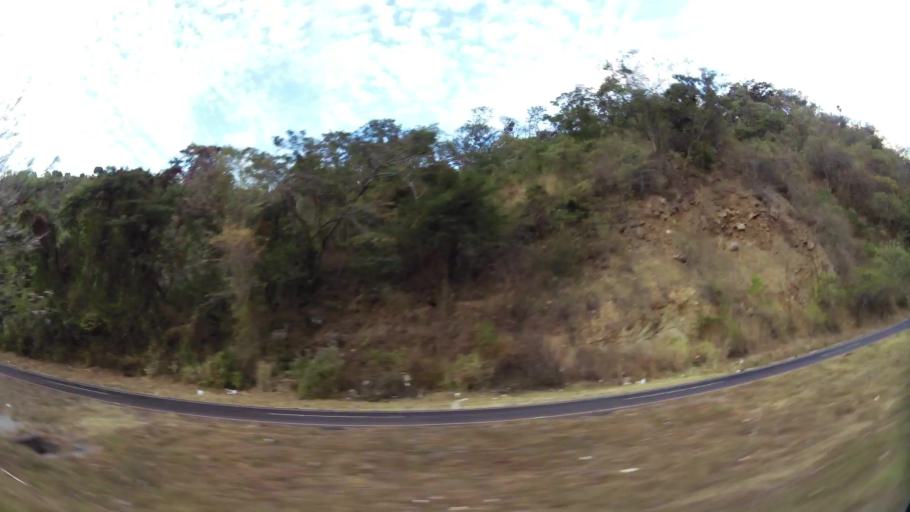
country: SV
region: San Vicente
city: Apastepeque
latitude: 13.6655
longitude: -88.8094
